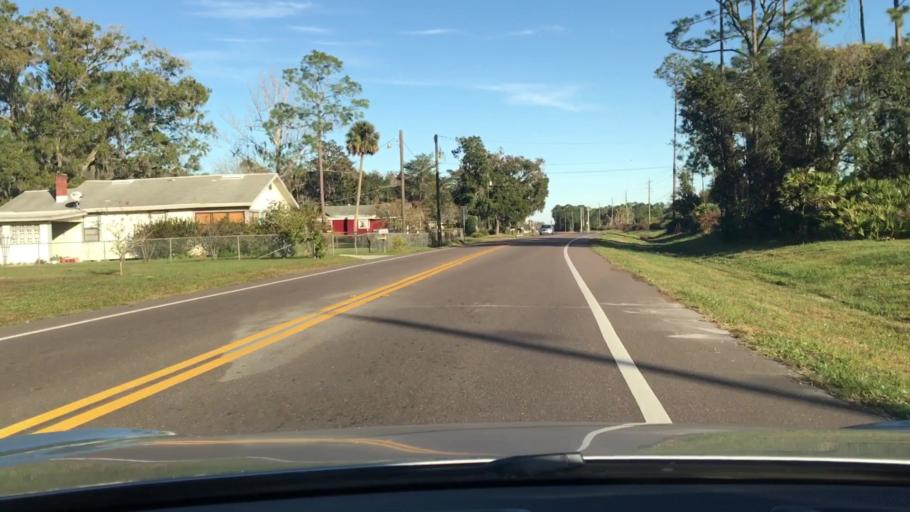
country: US
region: Florida
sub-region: Saint Johns County
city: Saint Augustine
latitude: 29.9309
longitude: -81.3646
